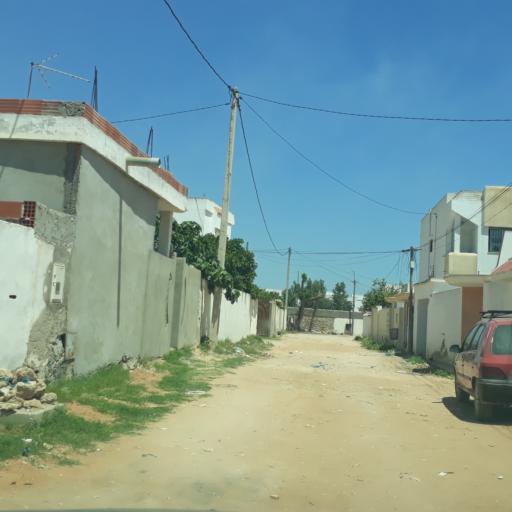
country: TN
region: Safaqis
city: Al Qarmadah
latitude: 34.8157
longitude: 10.7523
